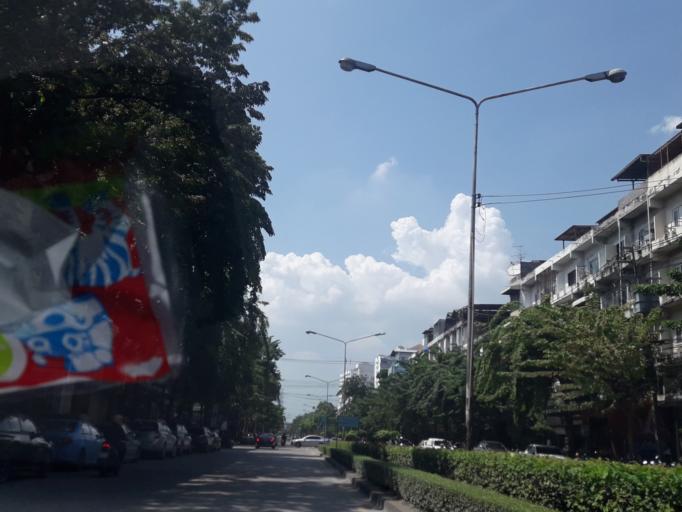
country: TH
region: Bangkok
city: Chatuchak
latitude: 13.8393
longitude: 100.5530
